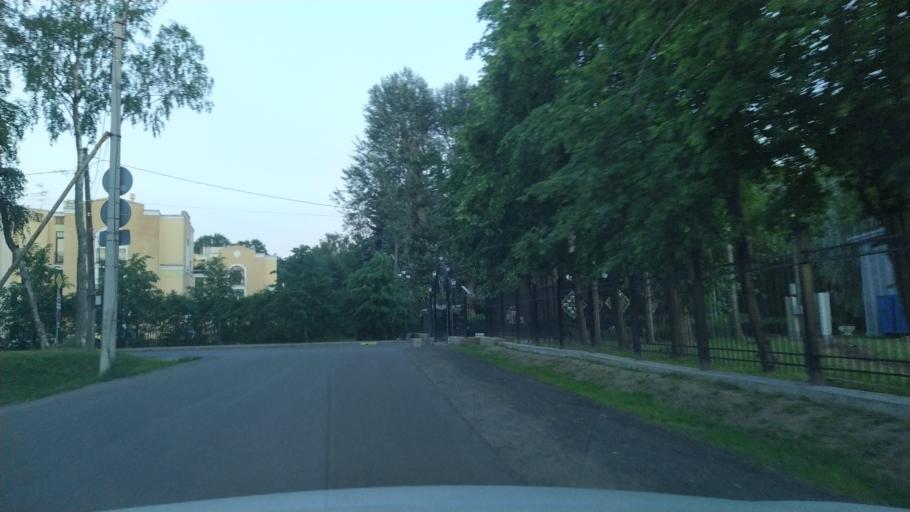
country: RU
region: St.-Petersburg
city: Sestroretsk
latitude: 60.0904
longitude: 29.9423
